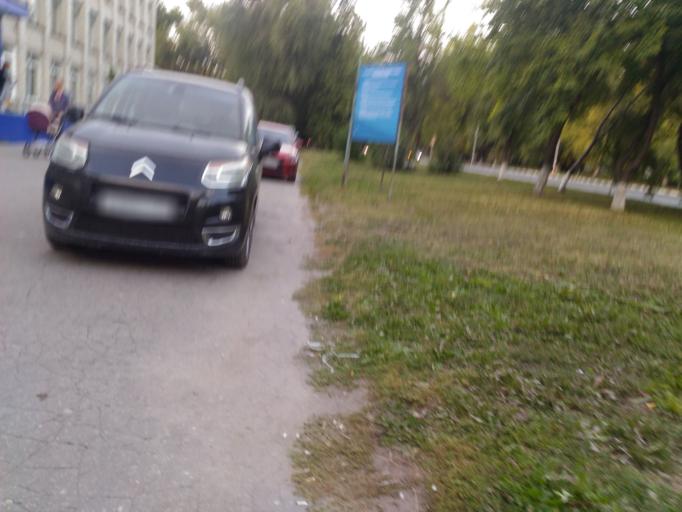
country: RU
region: Ulyanovsk
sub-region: Ulyanovskiy Rayon
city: Ulyanovsk
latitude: 54.2989
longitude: 48.3295
